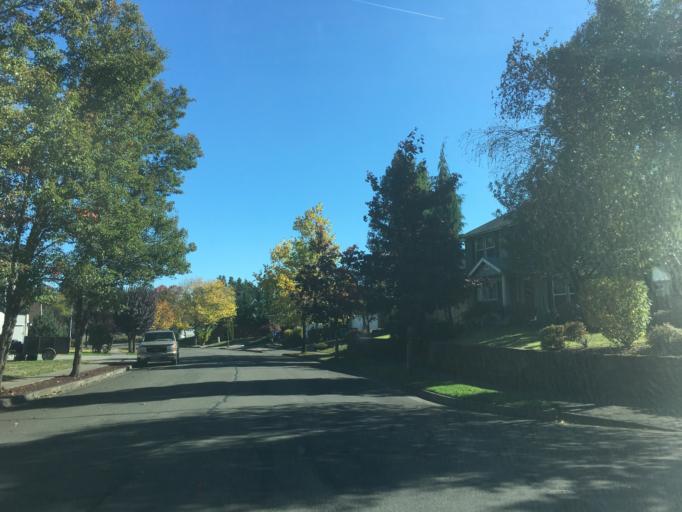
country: US
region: Oregon
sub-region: Multnomah County
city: Gresham
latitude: 45.4809
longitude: -122.4004
